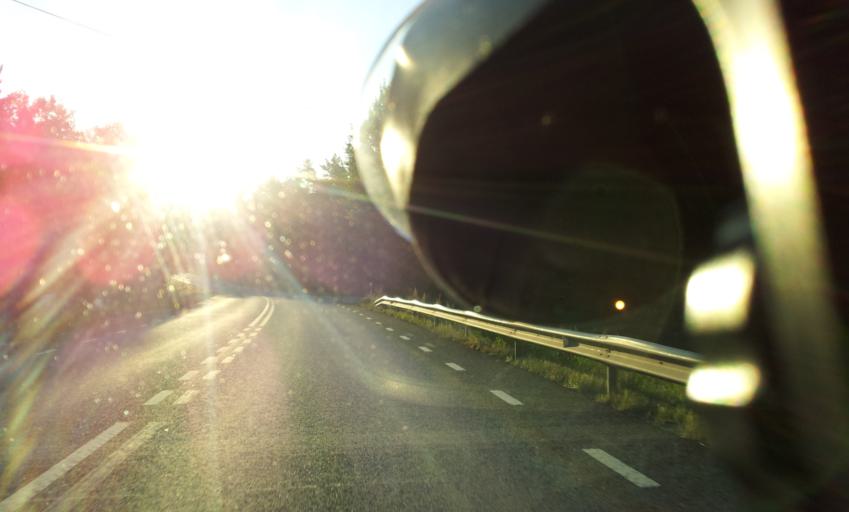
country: SE
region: Kalmar
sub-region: Vasterviks Kommun
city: Vaestervik
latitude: 57.7215
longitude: 16.4881
